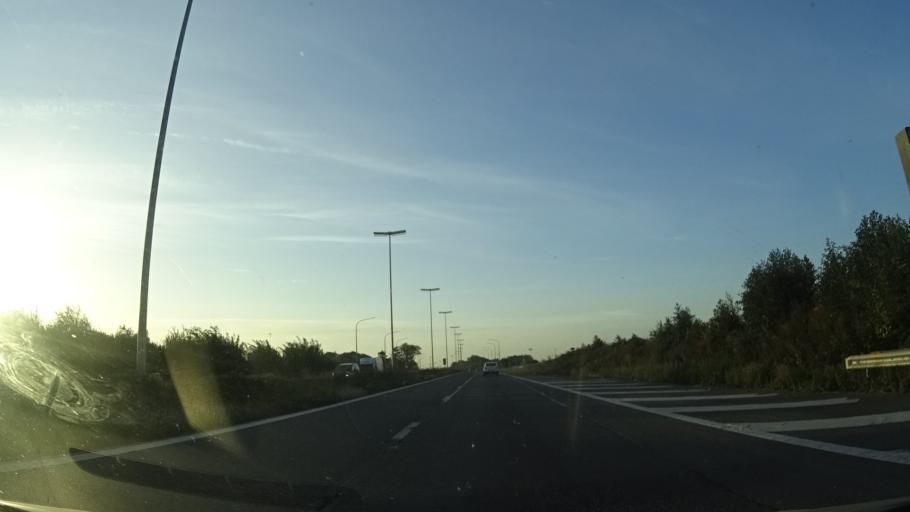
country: BE
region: Wallonia
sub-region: Province du Hainaut
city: Frameries
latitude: 50.4198
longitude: 3.9175
